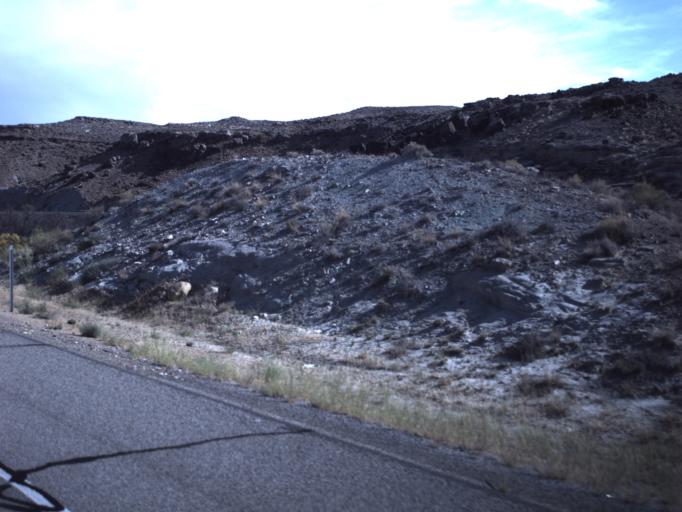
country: US
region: Utah
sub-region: Grand County
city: Moab
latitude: 38.7260
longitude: -109.7210
